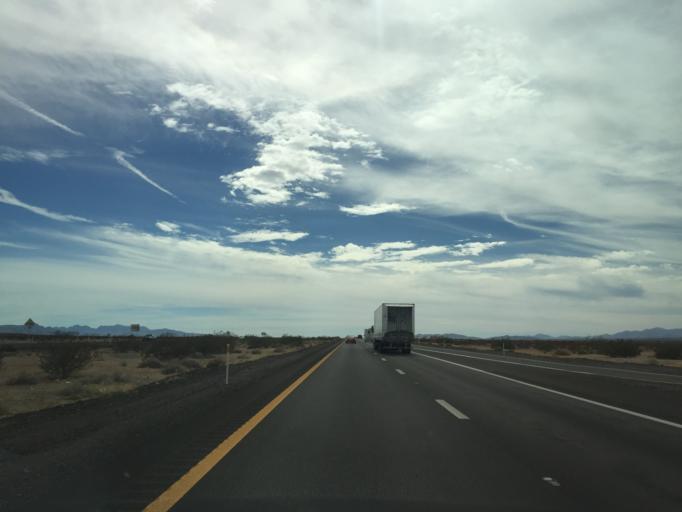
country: US
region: Nevada
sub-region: Clark County
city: Moapa Town
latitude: 36.5894
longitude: -114.6487
